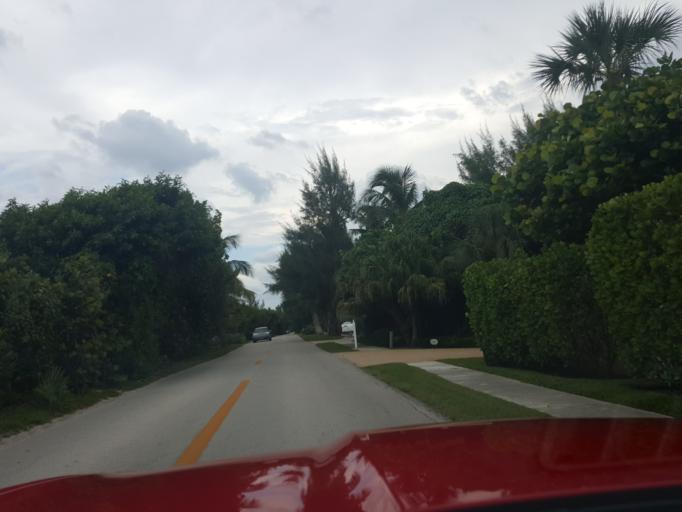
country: US
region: Florida
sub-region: Martin County
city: Hobe Sound
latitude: 27.0179
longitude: -80.0946
